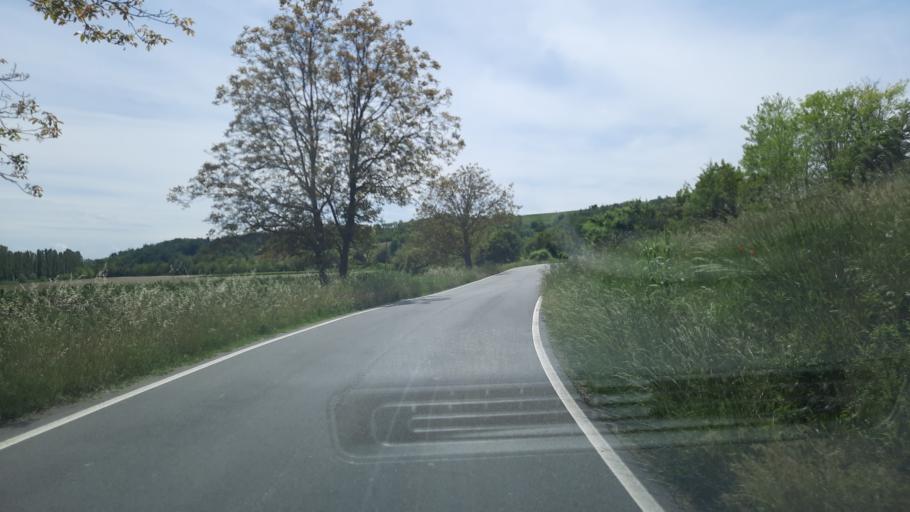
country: IT
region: Piedmont
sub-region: Provincia di Alessandria
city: Castelletto Merli
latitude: 45.0530
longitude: 8.2329
